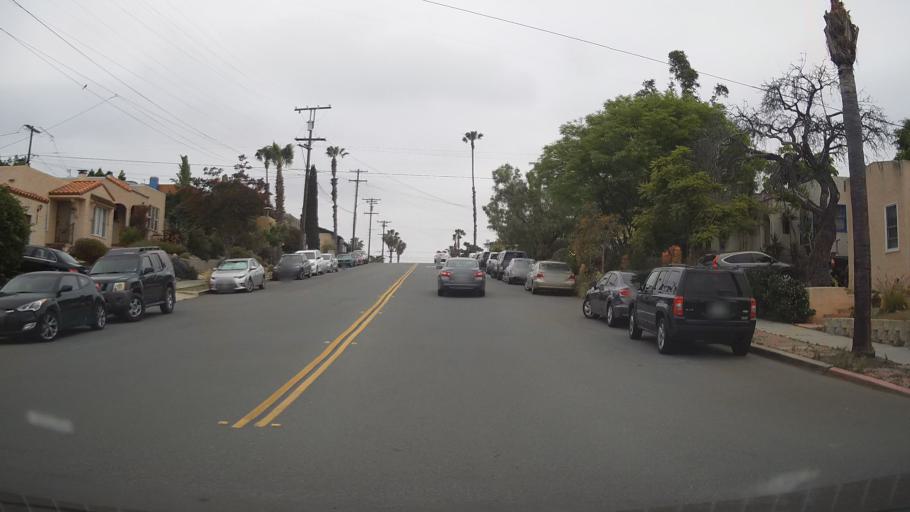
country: US
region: California
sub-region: San Diego County
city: San Diego
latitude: 32.7592
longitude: -117.1438
